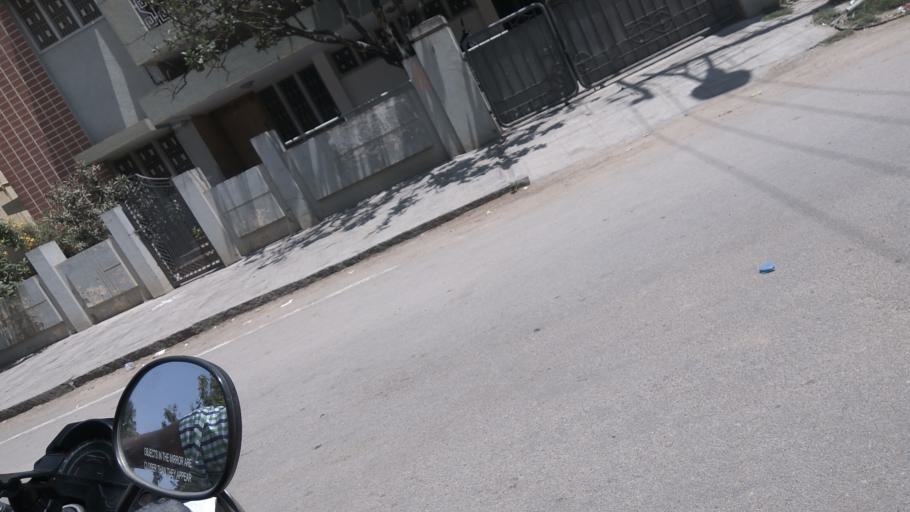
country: IN
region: Karnataka
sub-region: Kolar
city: Mulbagal
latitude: 13.1667
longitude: 78.3941
